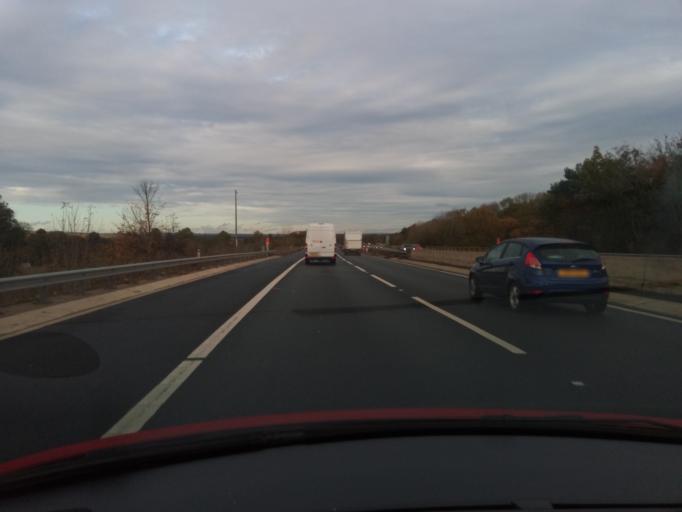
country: GB
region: England
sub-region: Darlington
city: High Coniscliffe
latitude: 54.4670
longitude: -1.6669
